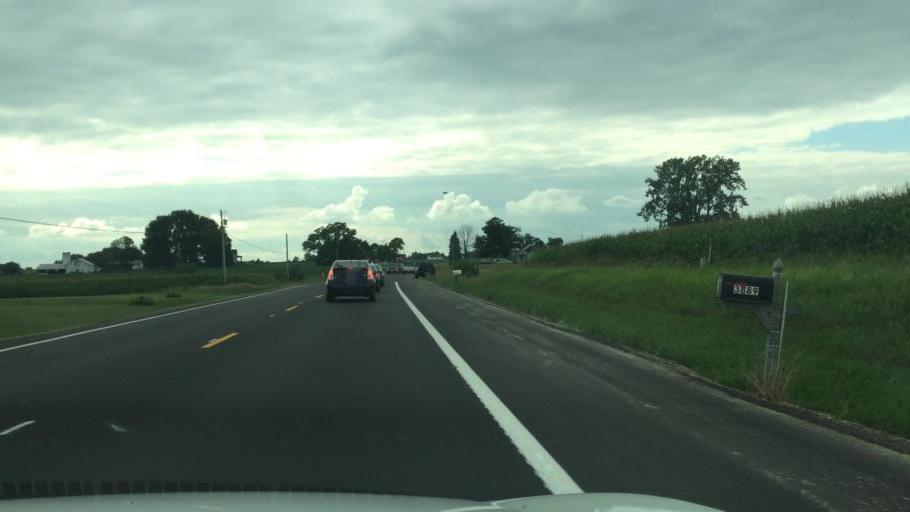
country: US
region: Ohio
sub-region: Champaign County
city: Urbana
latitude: 40.0857
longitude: -83.6781
